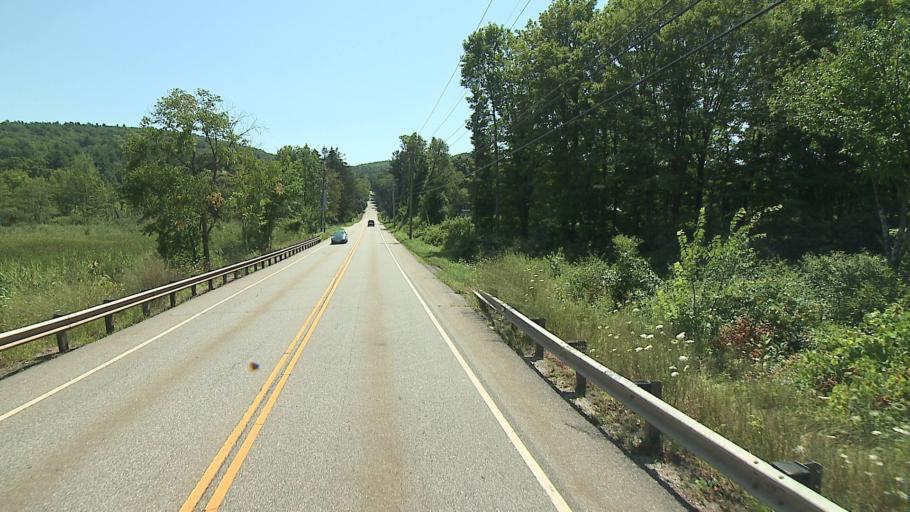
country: US
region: Connecticut
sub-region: Litchfield County
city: Litchfield
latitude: 41.8472
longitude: -73.3094
